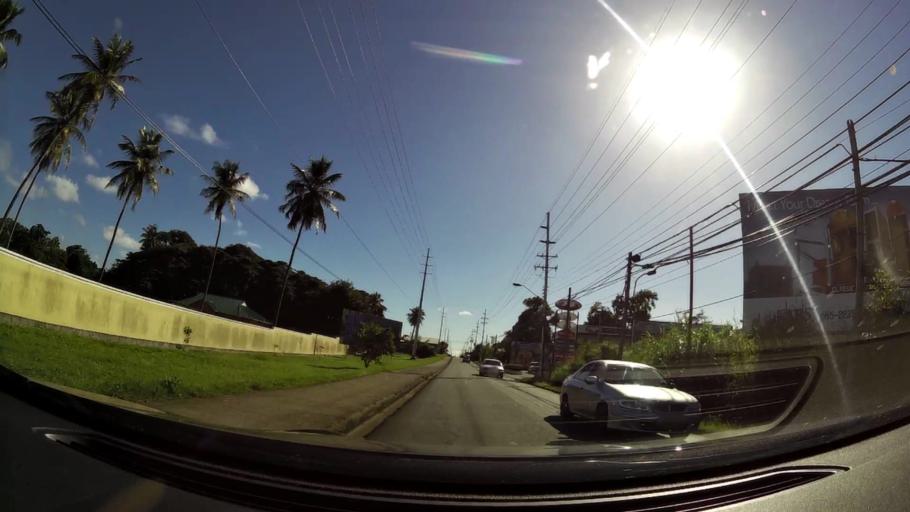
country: TT
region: Tobago
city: Scarborough
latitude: 11.1584
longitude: -60.8314
